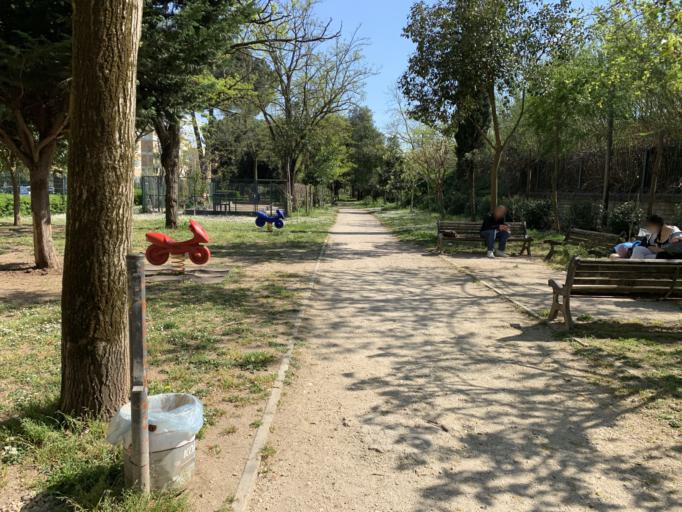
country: IT
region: Latium
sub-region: Citta metropolitana di Roma Capitale
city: Rome
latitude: 41.8626
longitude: 12.5454
